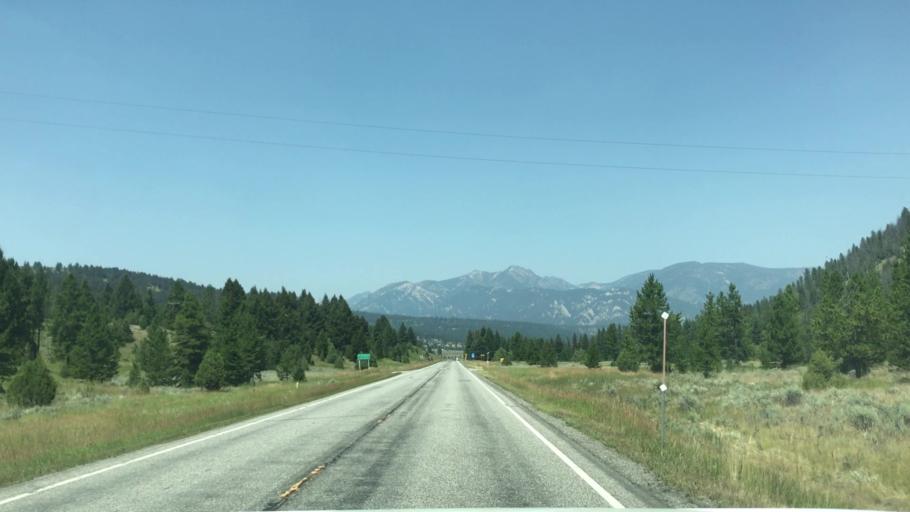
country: US
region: Montana
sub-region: Gallatin County
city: Big Sky
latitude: 45.2063
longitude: -111.2432
